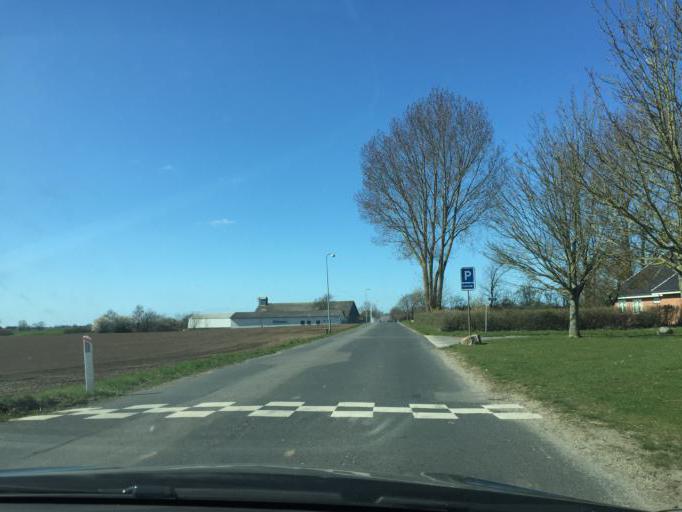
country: DK
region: South Denmark
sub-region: Faaborg-Midtfyn Kommune
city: Arslev
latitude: 55.3399
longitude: 10.5002
